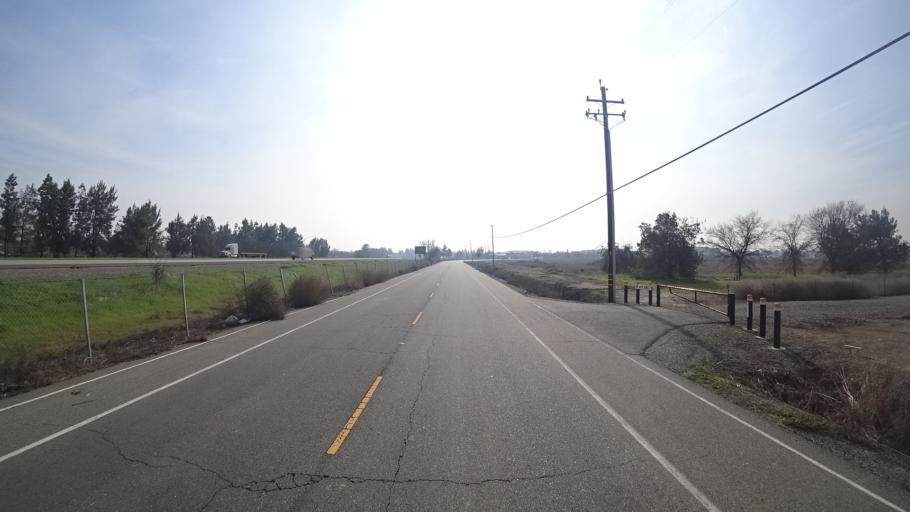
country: US
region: California
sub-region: Yolo County
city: Davis
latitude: 38.5673
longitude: -121.7682
